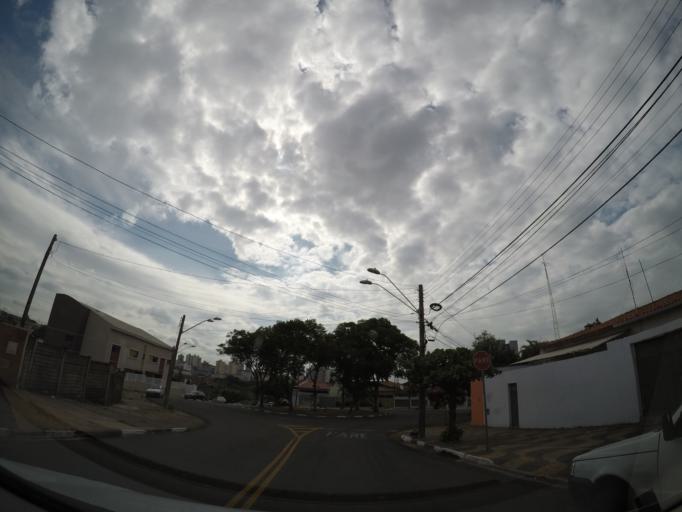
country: BR
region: Sao Paulo
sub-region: Campinas
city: Campinas
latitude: -22.9234
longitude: -47.0627
